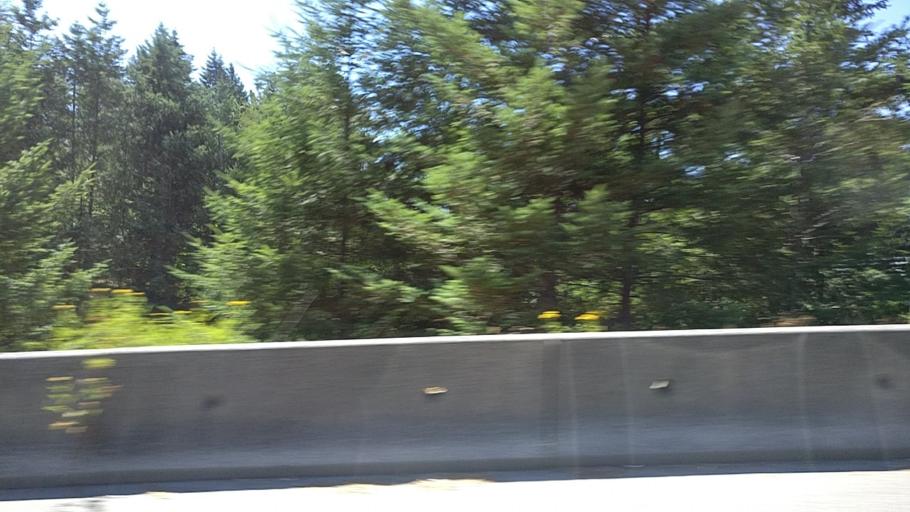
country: CA
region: British Columbia
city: Abbotsford
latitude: 49.0555
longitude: -122.2726
